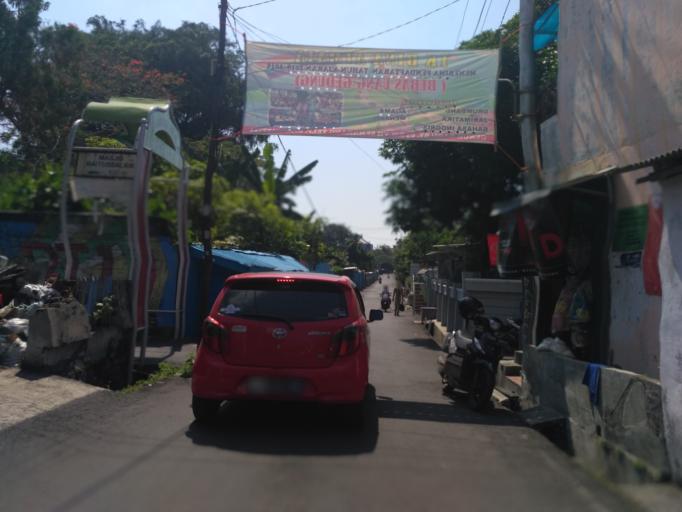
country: ID
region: Central Java
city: Semarang
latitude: -7.0049
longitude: 110.4246
